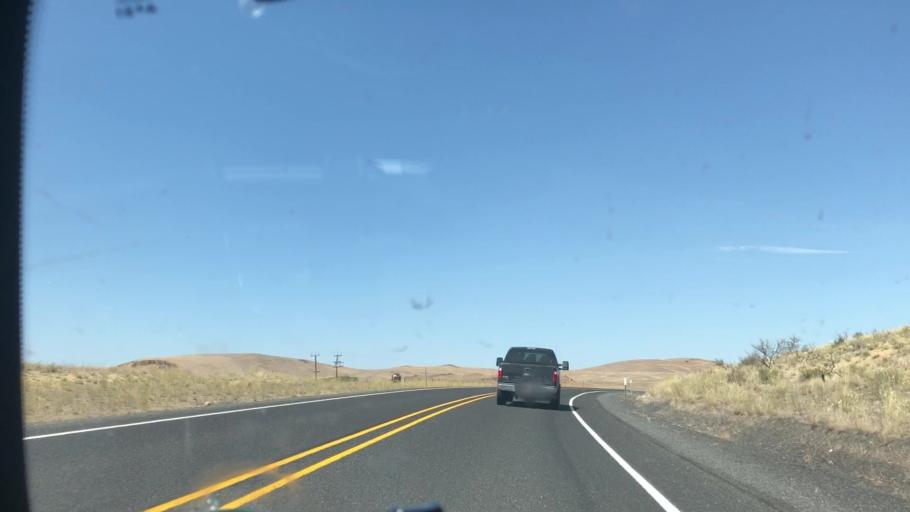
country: US
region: Idaho
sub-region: Owyhee County
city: Marsing
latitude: 43.2369
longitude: -117.0459
